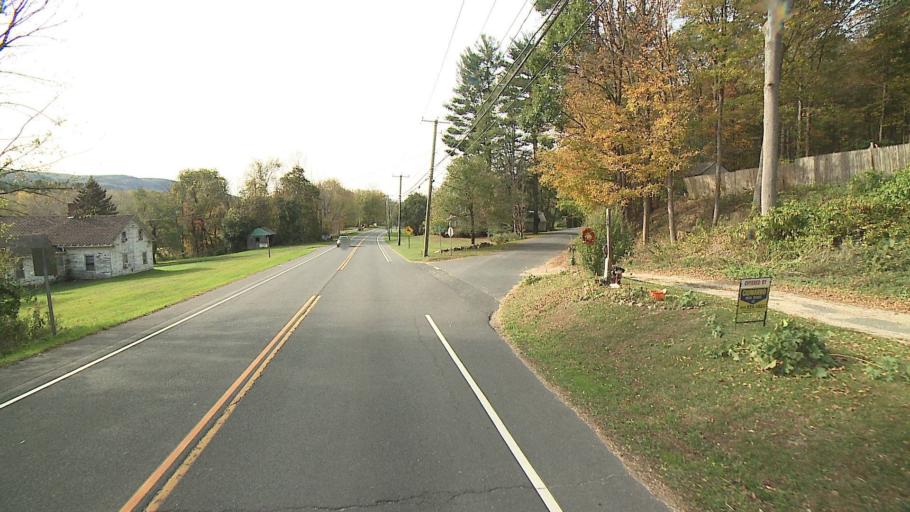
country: US
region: Connecticut
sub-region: Litchfield County
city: Canaan
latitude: 42.0066
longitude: -73.2541
